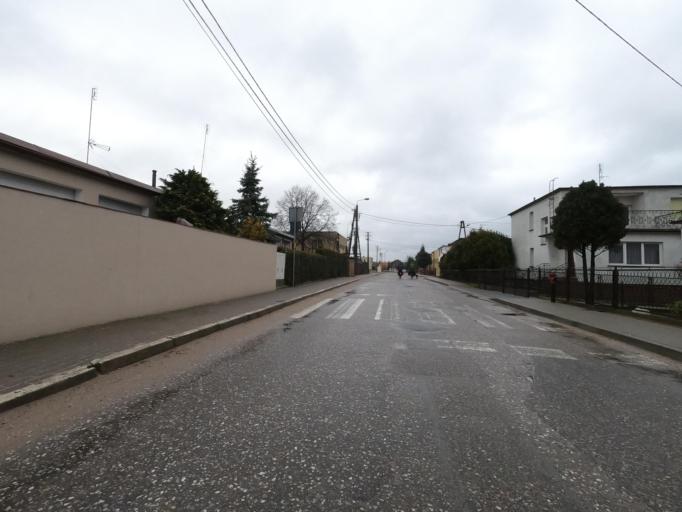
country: PL
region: Greater Poland Voivodeship
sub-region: Powiat pilski
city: Osiek nad Notecia
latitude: 53.1215
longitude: 17.2906
